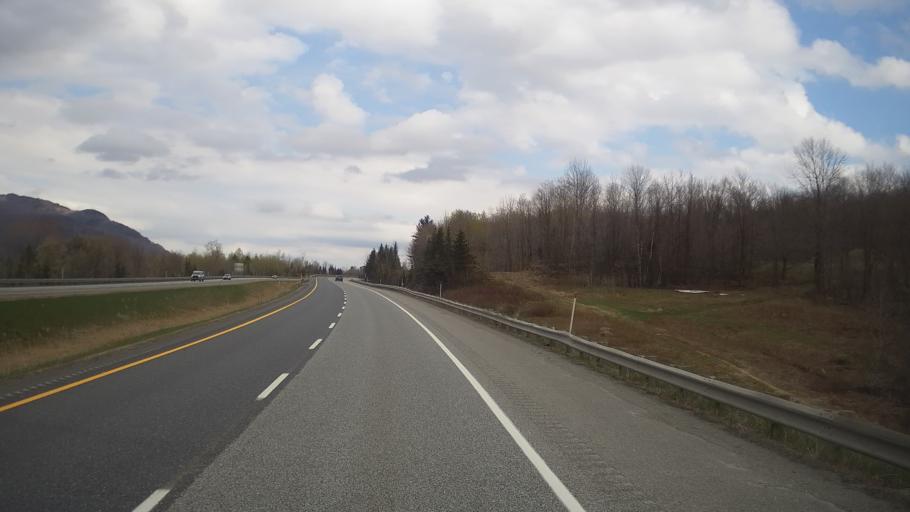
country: CA
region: Quebec
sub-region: Estrie
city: Magog
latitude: 45.2955
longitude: -72.2964
